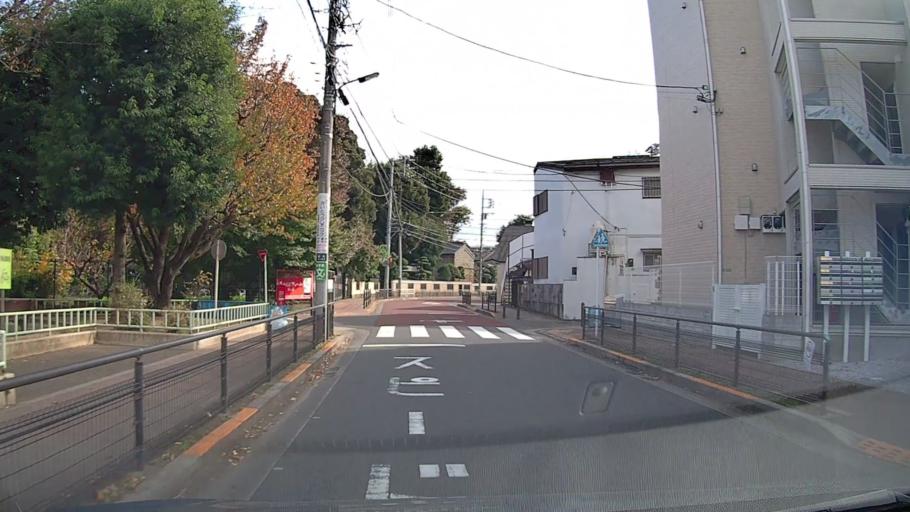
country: JP
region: Saitama
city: Wako
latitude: 35.7497
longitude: 139.6326
